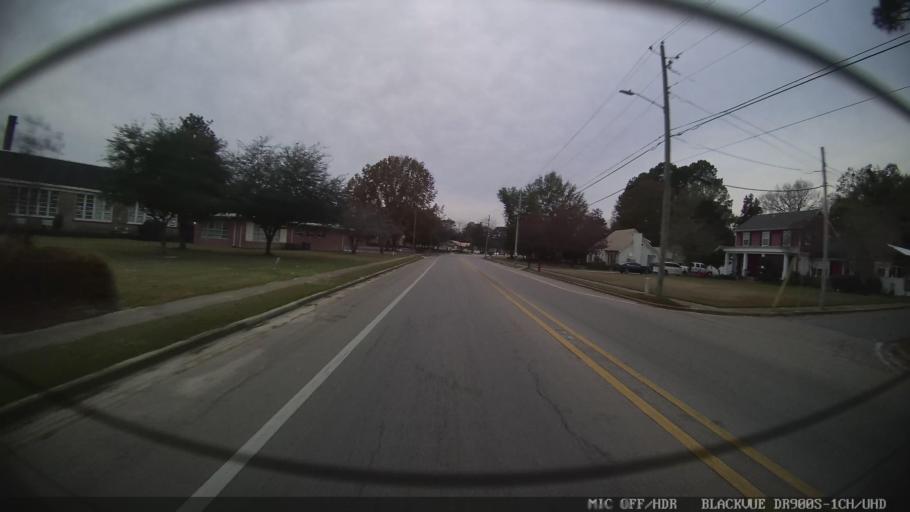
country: US
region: Mississippi
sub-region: Clarke County
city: Quitman
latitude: 32.0369
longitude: -88.7213
